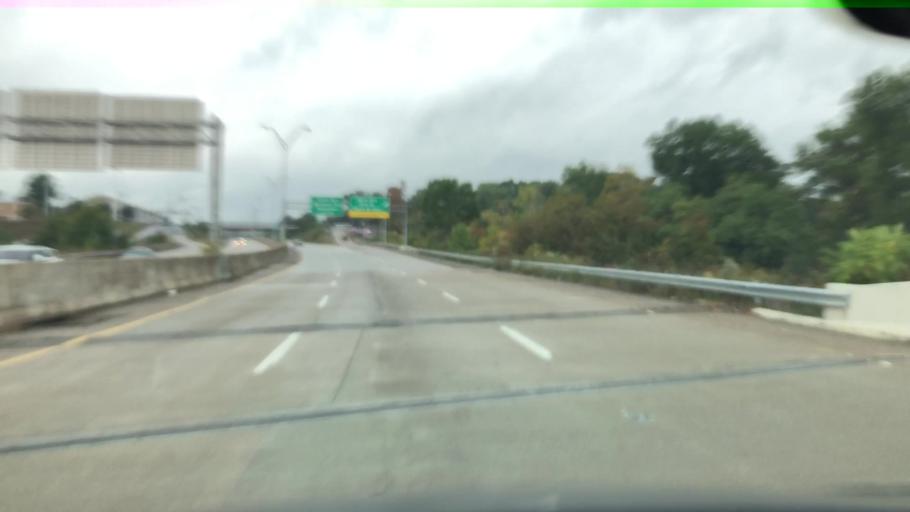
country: US
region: Ohio
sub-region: Mahoning County
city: Youngstown
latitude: 41.1060
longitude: -80.6385
